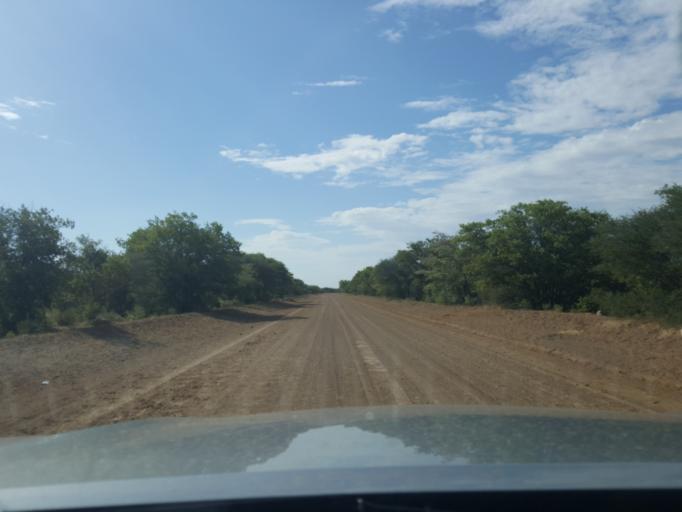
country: BW
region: Kweneng
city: Khudumelapye
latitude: -23.5336
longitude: 24.7256
